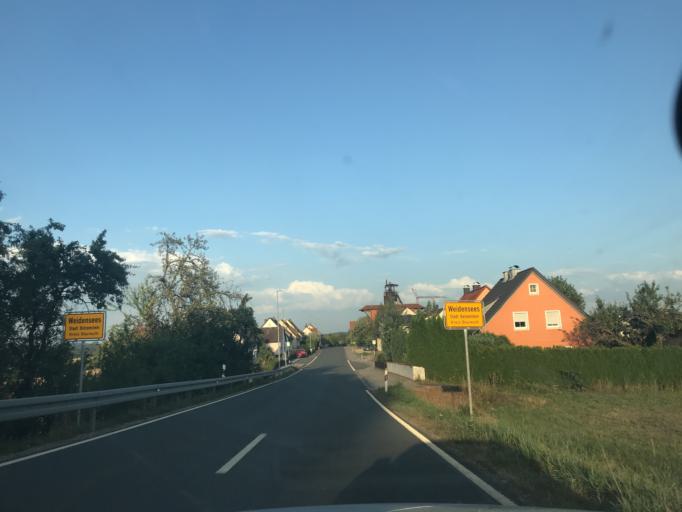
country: DE
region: Bavaria
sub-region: Upper Franconia
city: Pottenstein
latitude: 49.7117
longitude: 11.4347
